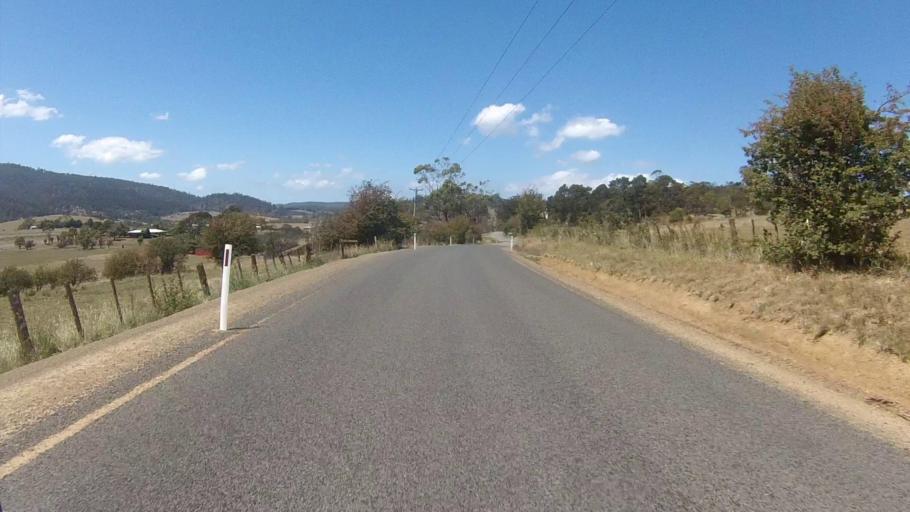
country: AU
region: Tasmania
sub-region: Sorell
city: Sorell
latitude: -42.7646
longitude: 147.6402
